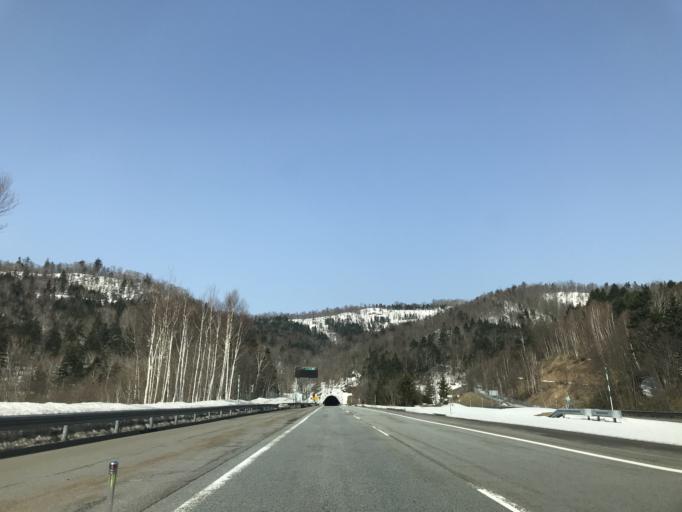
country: JP
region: Hokkaido
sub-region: Asahikawa-shi
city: Asahikawa
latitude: 43.7921
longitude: 142.2691
